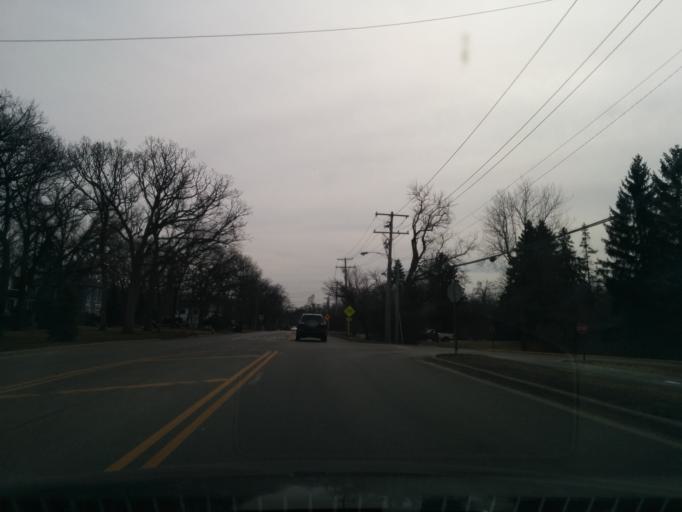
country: US
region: Illinois
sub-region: DuPage County
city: Oak Brook
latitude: 41.8315
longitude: -87.9286
